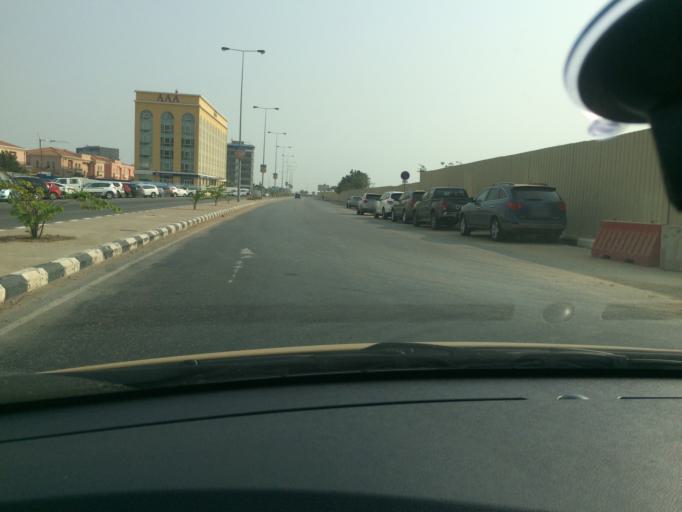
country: AO
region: Luanda
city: Luanda
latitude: -8.8150
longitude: 13.2205
